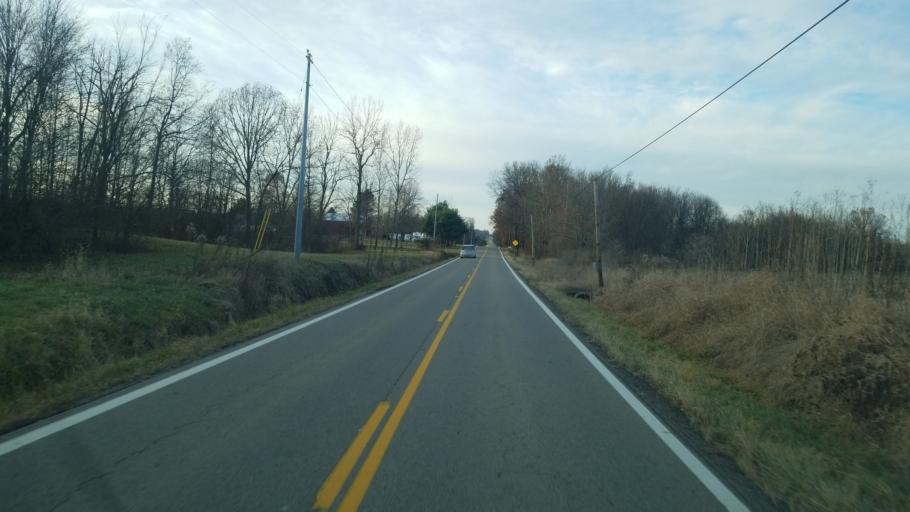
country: US
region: Ohio
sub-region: Licking County
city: Utica
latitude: 40.1849
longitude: -82.5120
